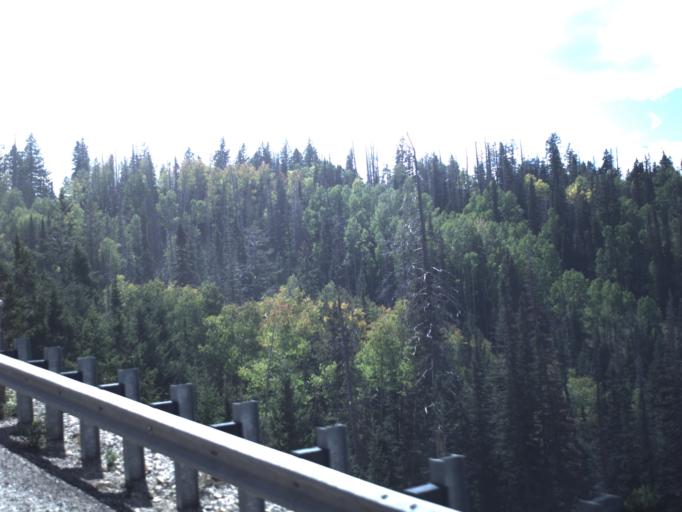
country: US
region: Utah
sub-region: Iron County
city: Cedar City
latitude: 37.5848
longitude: -112.8838
